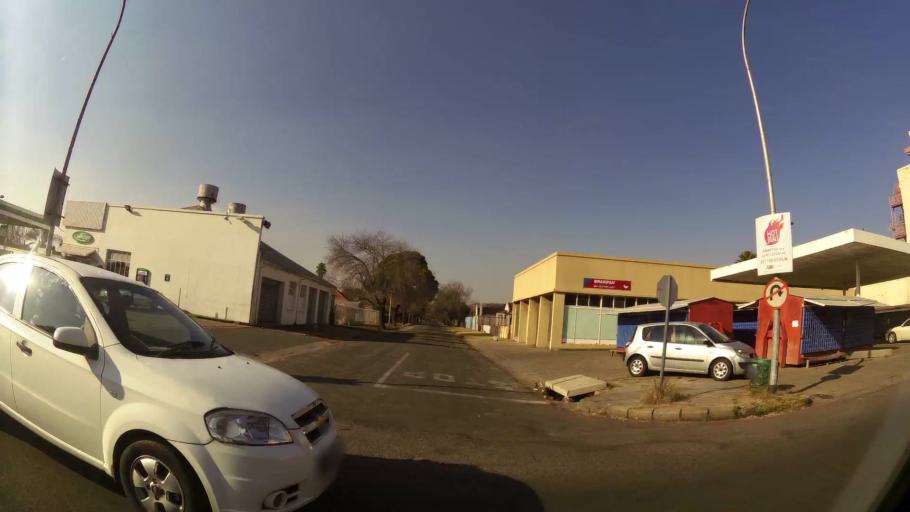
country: ZA
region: Gauteng
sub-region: Ekurhuleni Metropolitan Municipality
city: Brakpan
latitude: -26.2425
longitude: 28.3676
